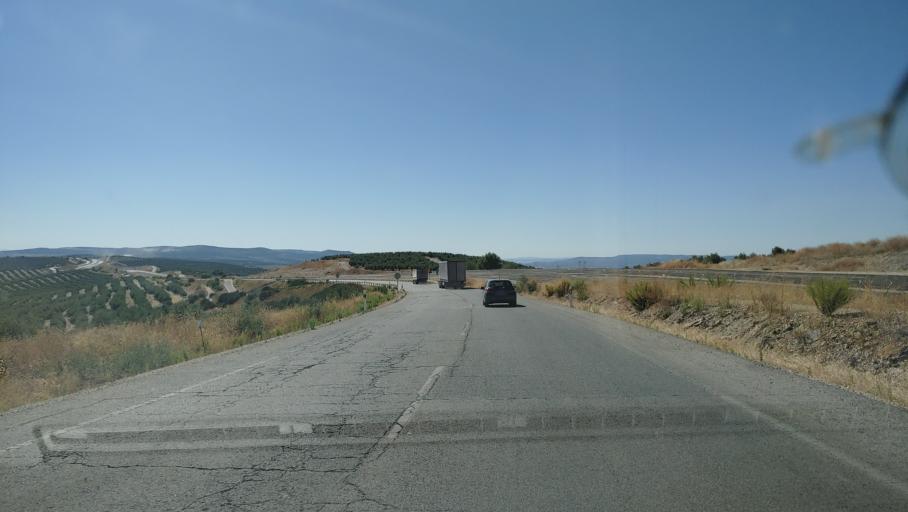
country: ES
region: Andalusia
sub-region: Provincia de Jaen
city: Villacarrillo
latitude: 38.1058
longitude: -3.1169
